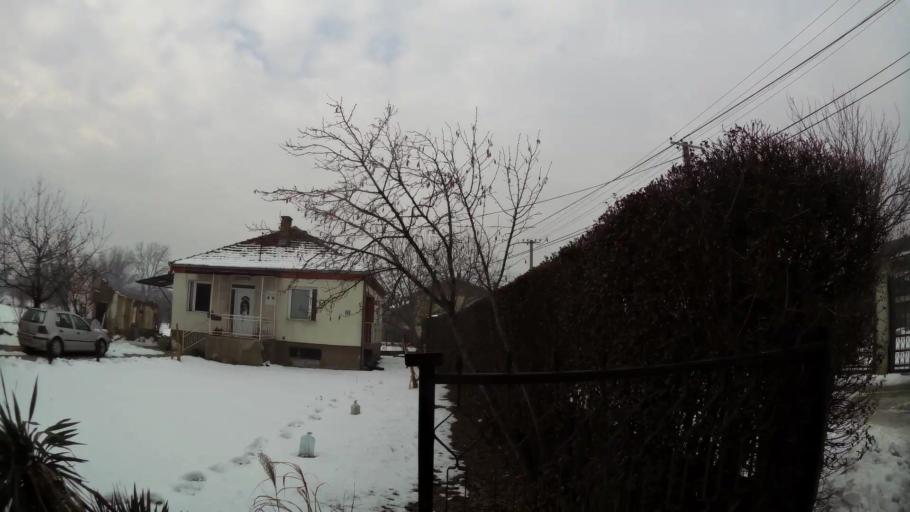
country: MK
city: Kondovo
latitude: 42.0446
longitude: 21.3495
